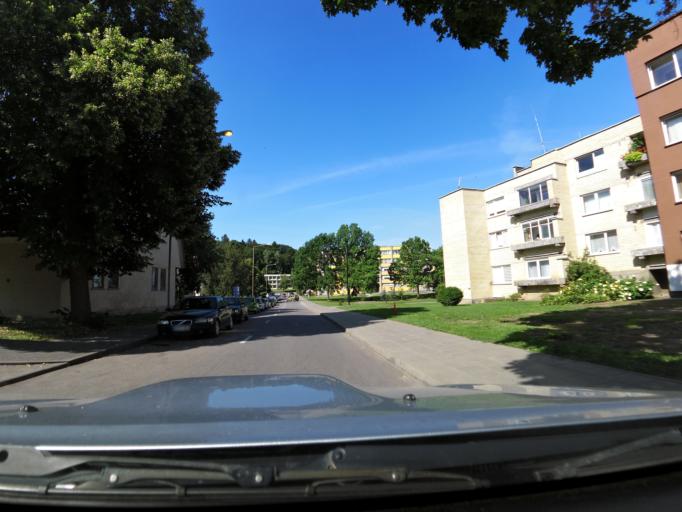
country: LT
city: Birstonas
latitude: 54.6027
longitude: 24.0311
